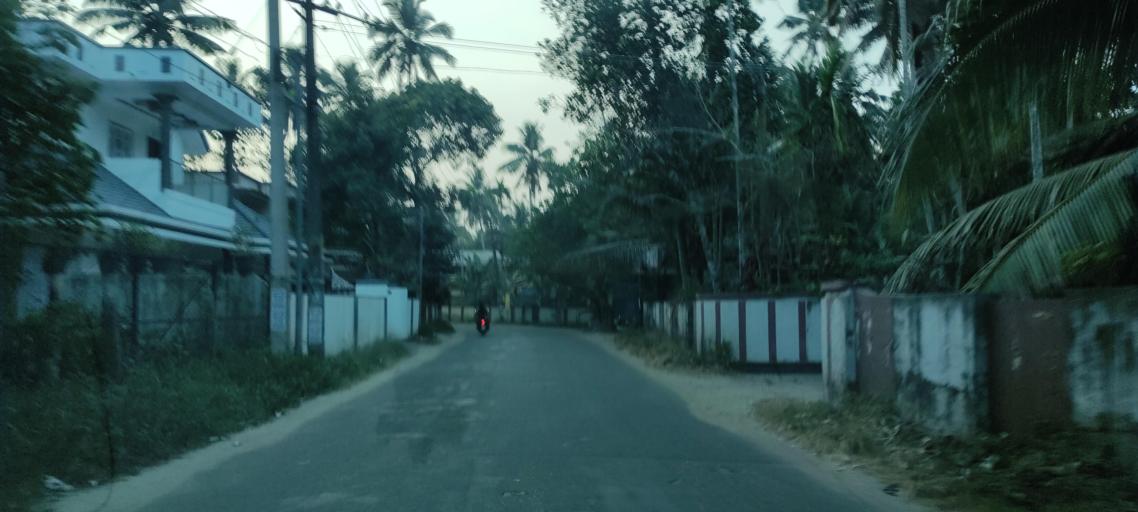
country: IN
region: Kerala
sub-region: Alappuzha
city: Kayankulam
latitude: 9.1209
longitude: 76.4927
